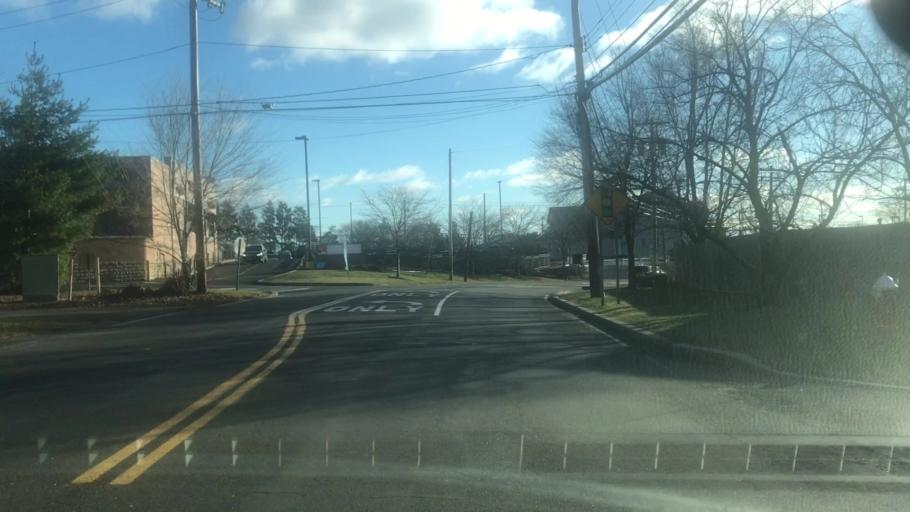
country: US
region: New York
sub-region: Rockland County
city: West Haverstraw
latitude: 41.2191
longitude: -73.9881
